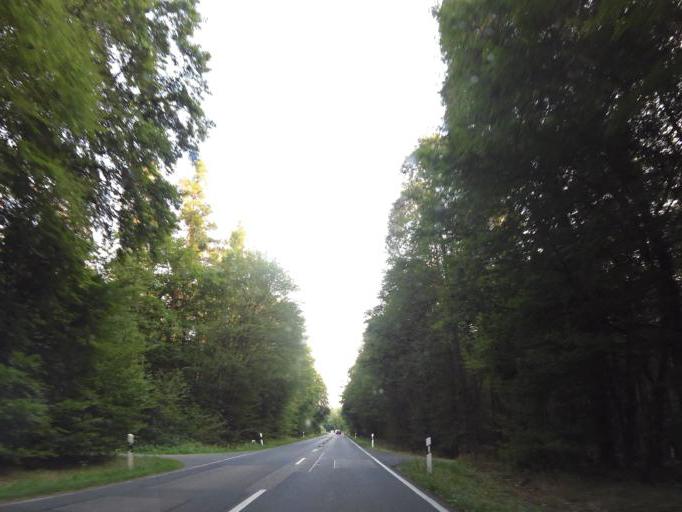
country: DE
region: Hesse
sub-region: Regierungsbezirk Darmstadt
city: Buttelborn
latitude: 49.9489
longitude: 8.5421
